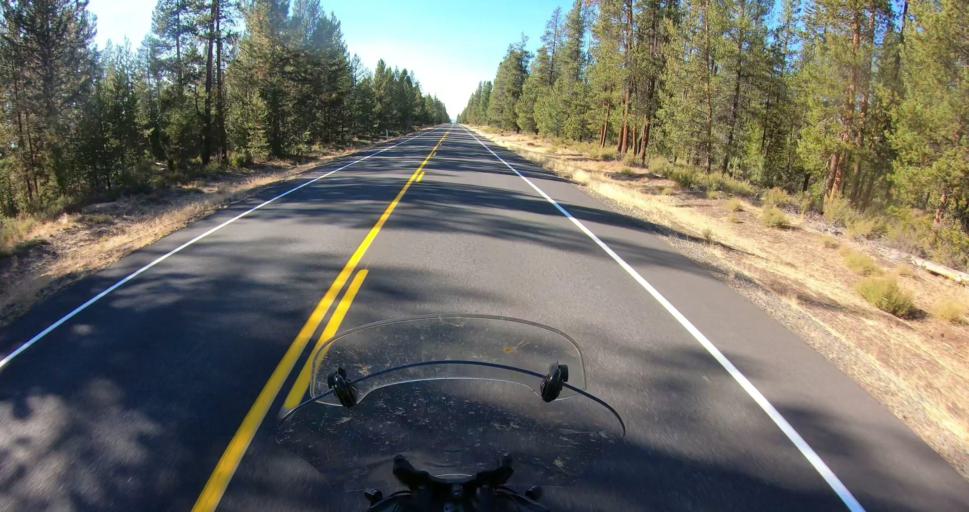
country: US
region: Oregon
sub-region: Deschutes County
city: La Pine
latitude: 43.4798
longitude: -121.4160
